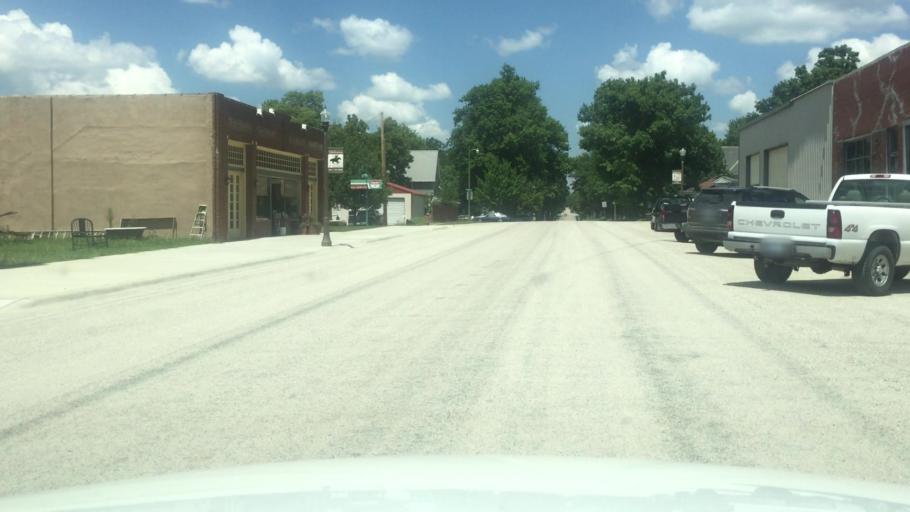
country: US
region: Kansas
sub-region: Brown County
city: Horton
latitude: 39.6614
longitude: -95.5274
